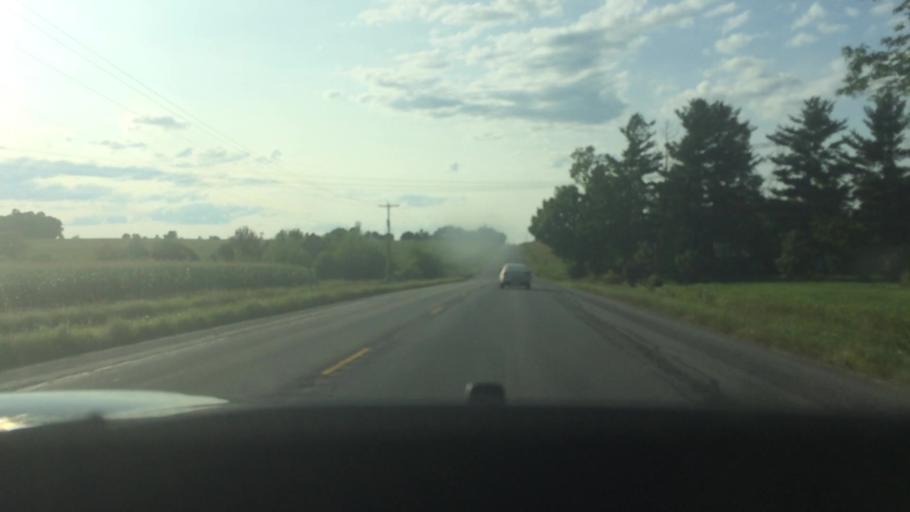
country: US
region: New York
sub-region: St. Lawrence County
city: Canton
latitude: 44.5977
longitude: -75.1914
